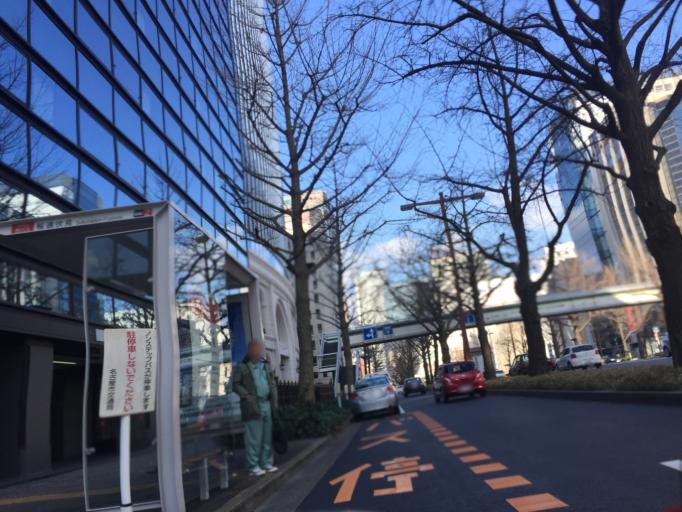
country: JP
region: Aichi
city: Nagoya-shi
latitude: 35.1727
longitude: 136.8957
